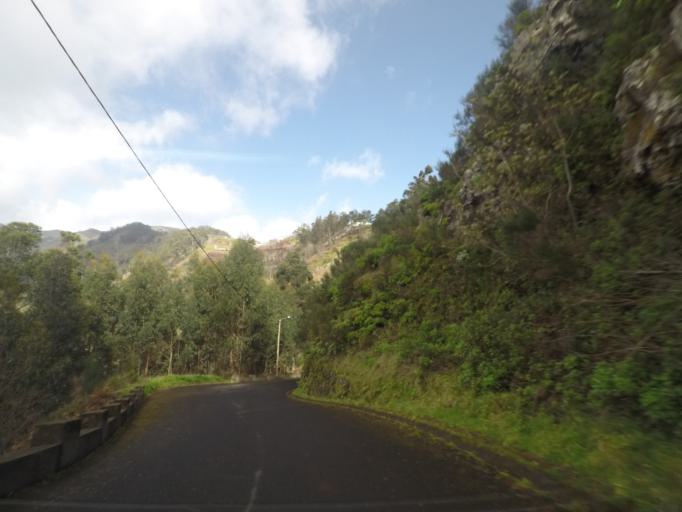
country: PT
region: Madeira
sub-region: Ribeira Brava
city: Campanario
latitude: 32.6984
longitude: -17.0281
